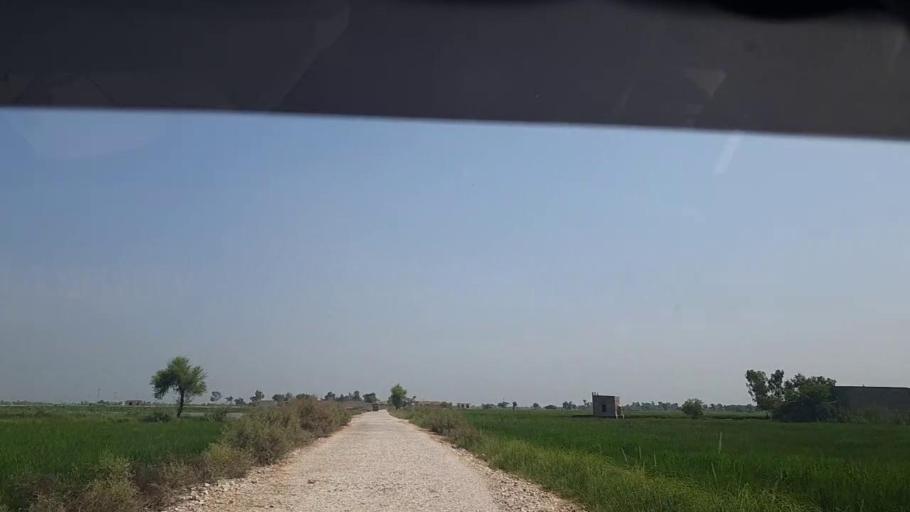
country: PK
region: Sindh
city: Thul
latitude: 28.1971
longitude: 68.7321
